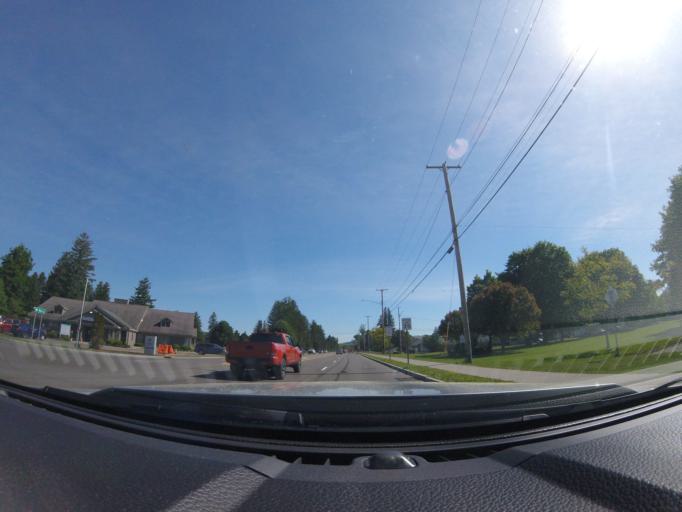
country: US
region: New York
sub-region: Cortland County
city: Cortland
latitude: 42.6045
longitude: -76.2001
